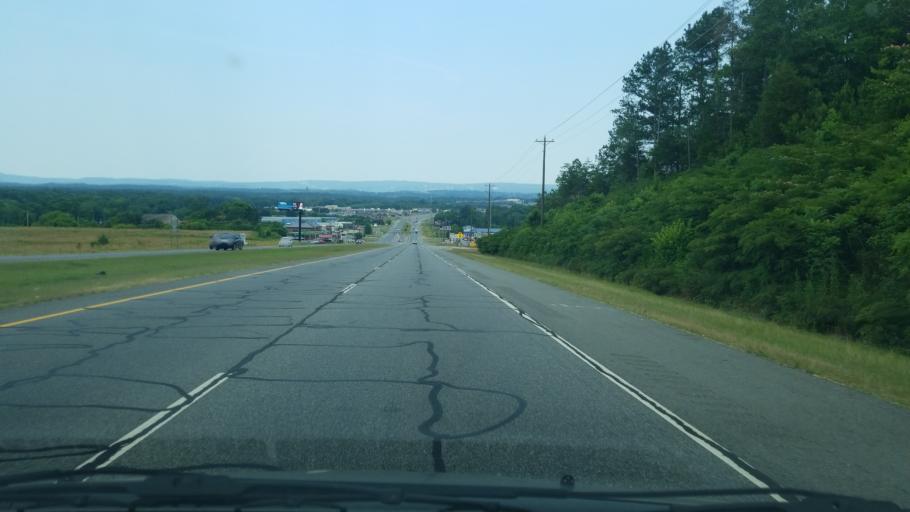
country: US
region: Georgia
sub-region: Catoosa County
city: Indian Springs
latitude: 34.9363
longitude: -85.2010
